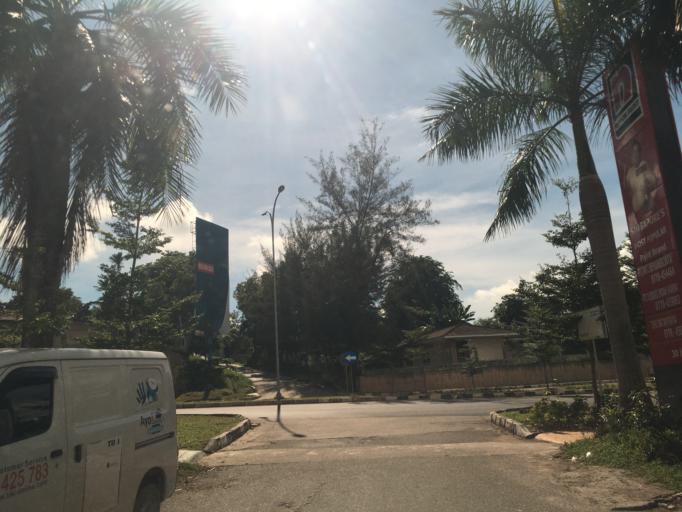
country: SG
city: Singapore
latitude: 1.1501
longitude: 104.0118
